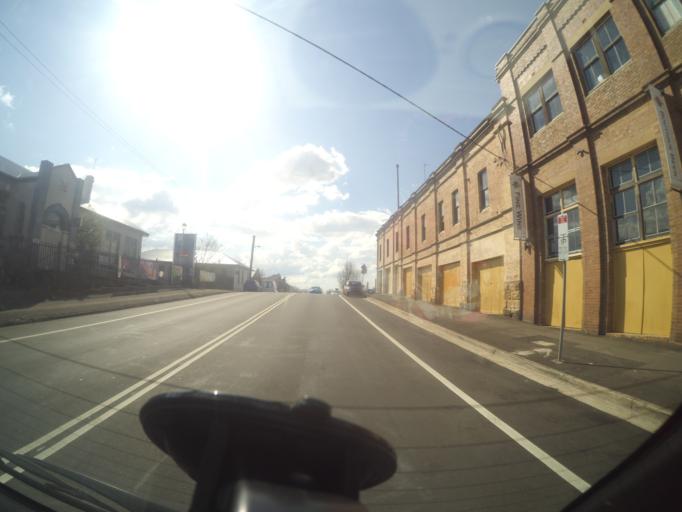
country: AU
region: New South Wales
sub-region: Blue Mountains Municipality
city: Katoomba
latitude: -33.7131
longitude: 150.3101
